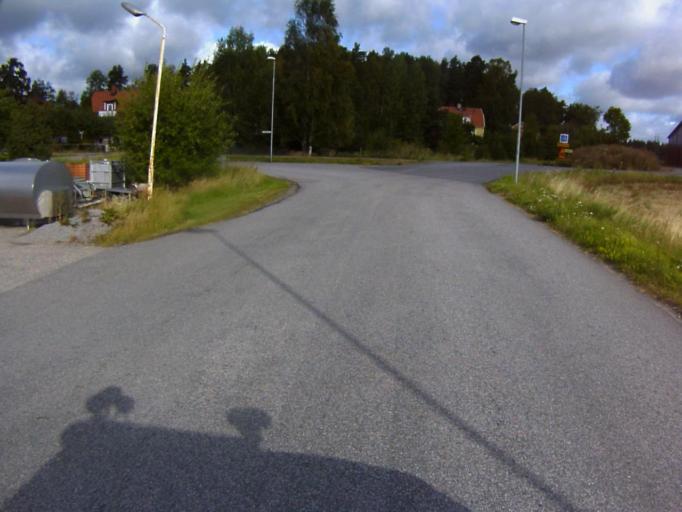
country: SE
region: Soedermanland
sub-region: Eskilstuna Kommun
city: Eskilstuna
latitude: 59.3747
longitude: 16.5627
